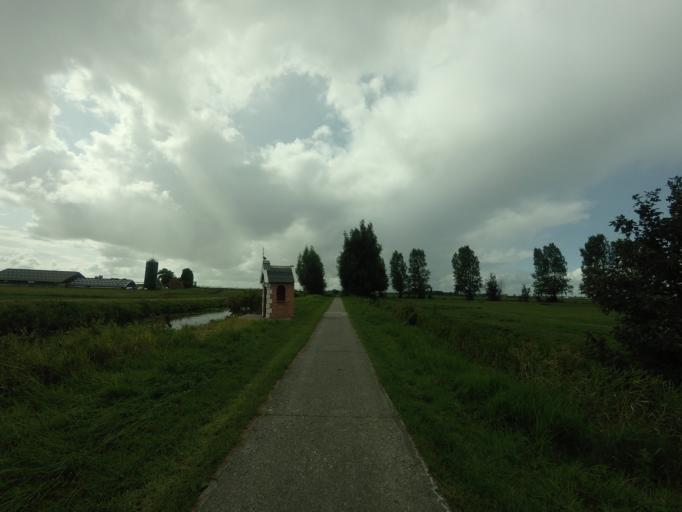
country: NL
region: Friesland
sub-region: Gemeente Boarnsterhim
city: Wergea
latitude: 53.1466
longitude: 5.8254
